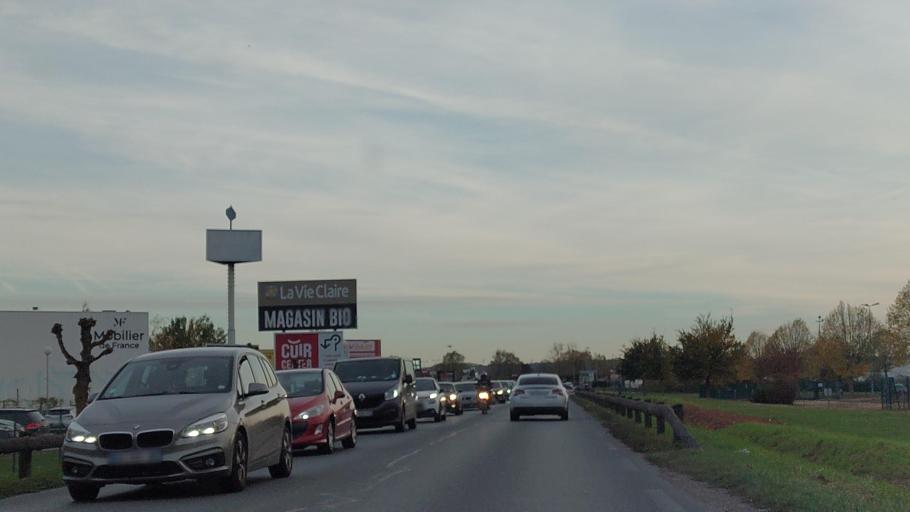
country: FR
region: Ile-de-France
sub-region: Departement de Seine-et-Marne
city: Claye-Souilly
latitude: 48.9512
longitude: 2.6665
